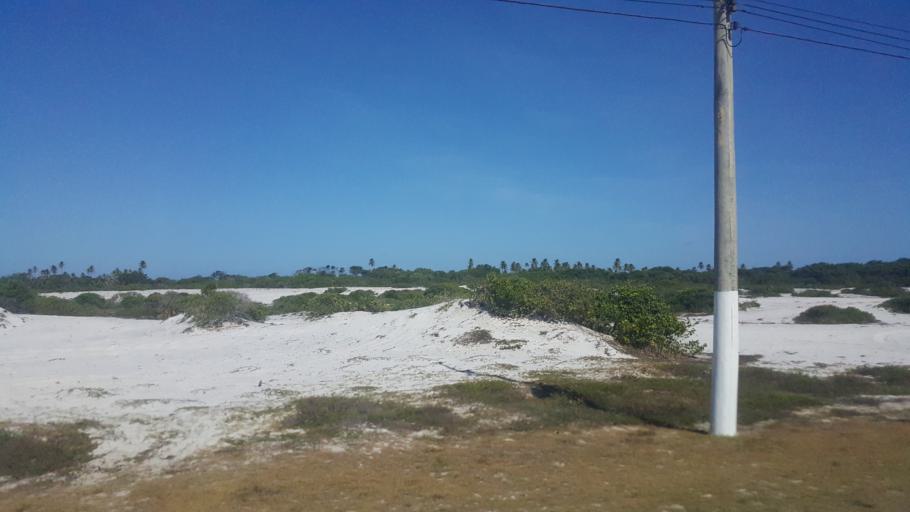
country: BR
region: Bahia
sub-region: Mata De Sao Joao
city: Mata de Sao Joao
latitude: -12.4335
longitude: -37.9200
